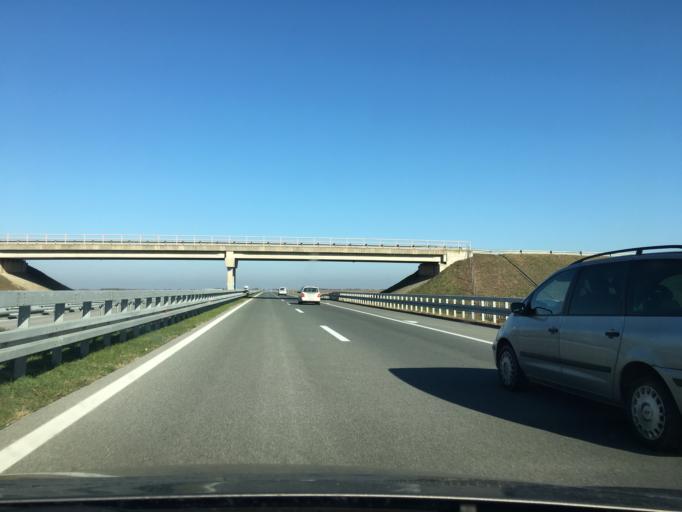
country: RS
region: Autonomna Pokrajina Vojvodina
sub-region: Severnobacki Okrug
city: Mali Igos
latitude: 45.7480
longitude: 19.7025
